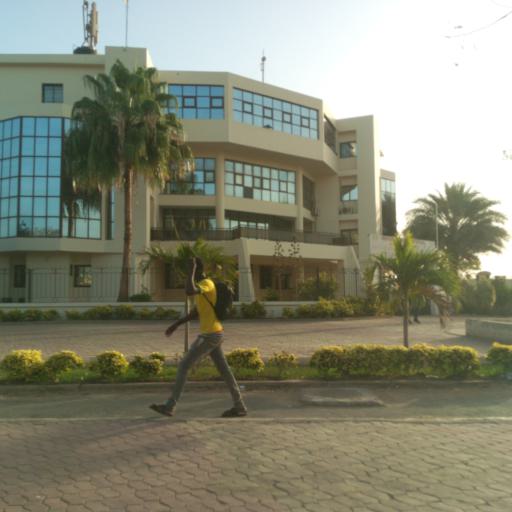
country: SN
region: Dakar
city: Dakar
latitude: 14.6971
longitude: -17.4516
